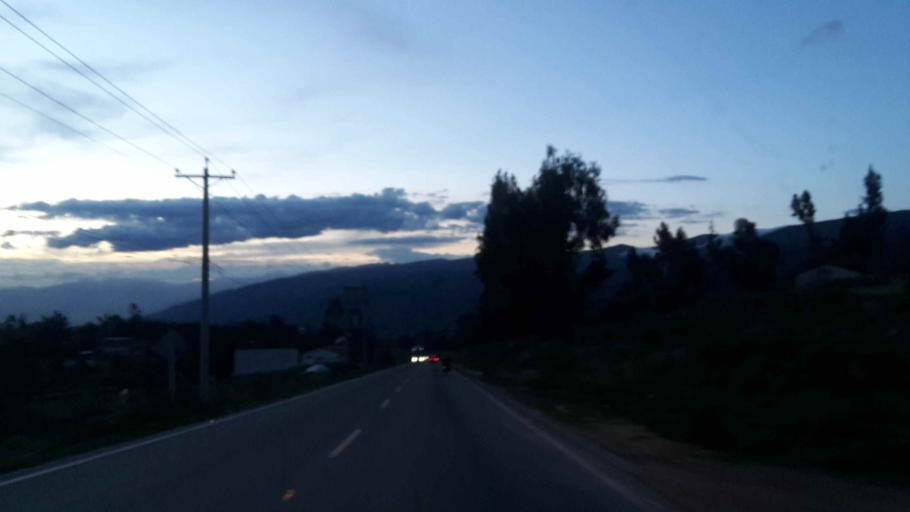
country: BO
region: Cochabamba
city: Colomi
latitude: -17.4266
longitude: -65.9196
